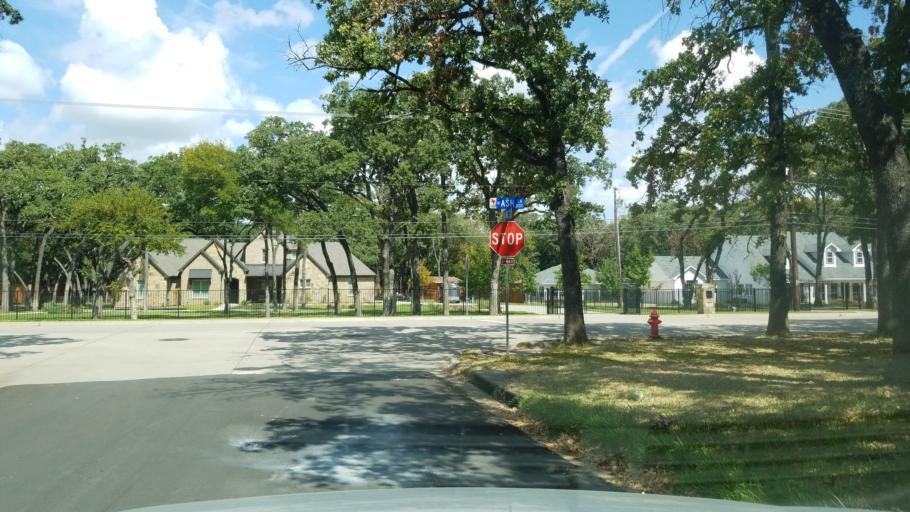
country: US
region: Texas
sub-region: Tarrant County
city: Euless
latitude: 32.8588
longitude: -97.0863
